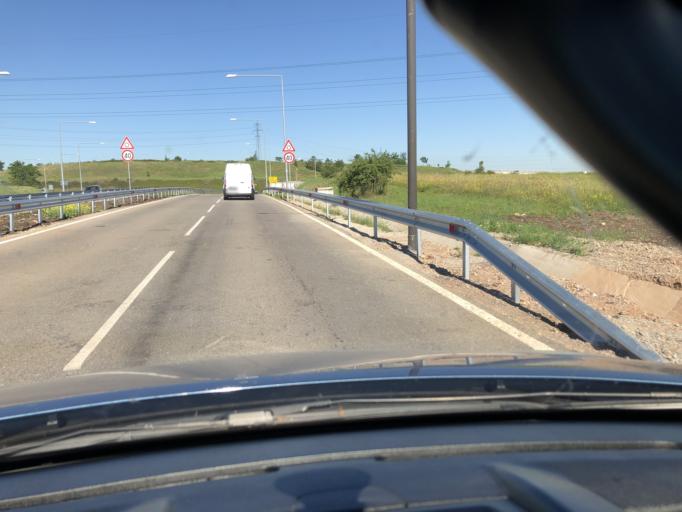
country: BG
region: Sofiya
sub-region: Obshtina Bozhurishte
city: Bozhurishte
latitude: 42.7127
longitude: 23.2339
